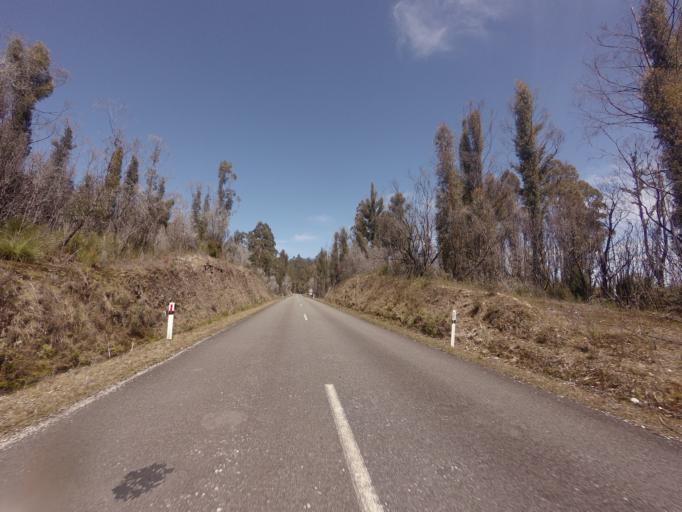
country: AU
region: Tasmania
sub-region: Huon Valley
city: Geeveston
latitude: -42.8336
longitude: 146.2678
